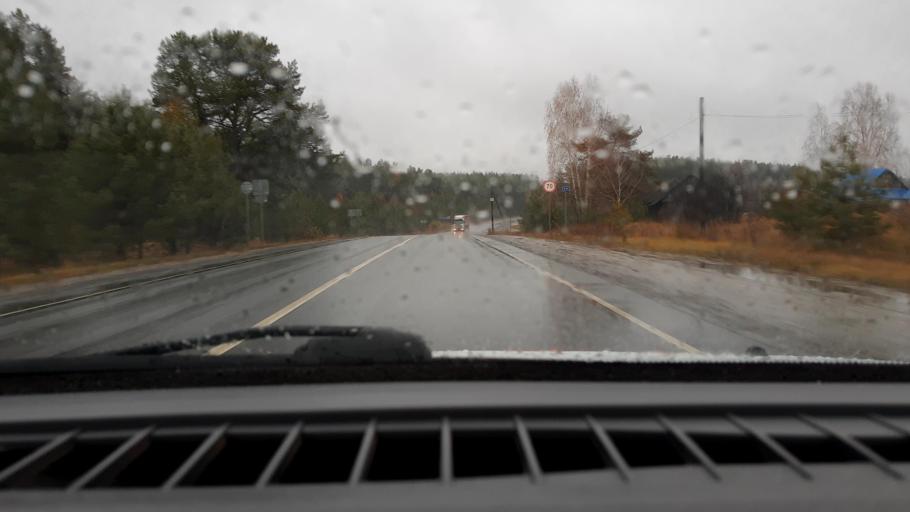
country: RU
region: Nizjnij Novgorod
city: Linda
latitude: 56.6901
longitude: 44.1869
